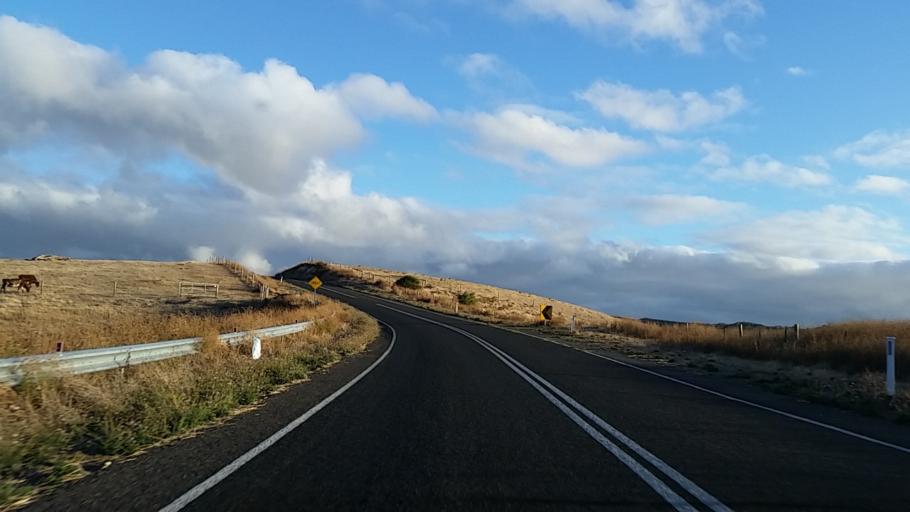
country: AU
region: South Australia
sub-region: Yankalilla
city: Normanville
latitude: -35.5442
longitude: 138.1936
